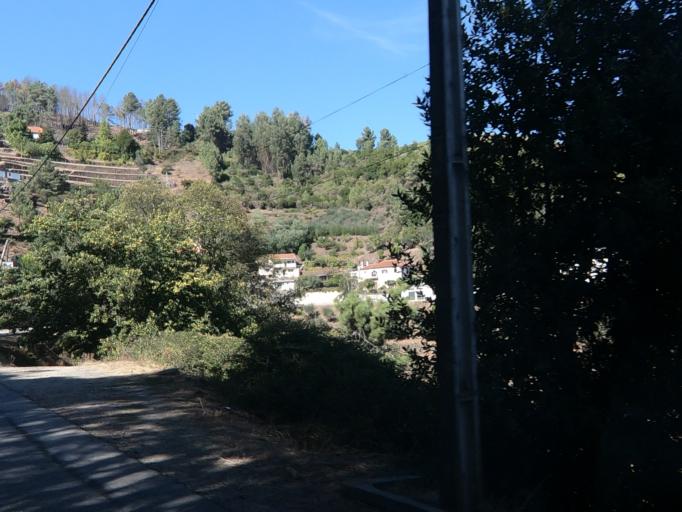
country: PT
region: Vila Real
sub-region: Santa Marta de Penaguiao
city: Santa Marta de Penaguiao
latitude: 41.2305
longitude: -7.7930
